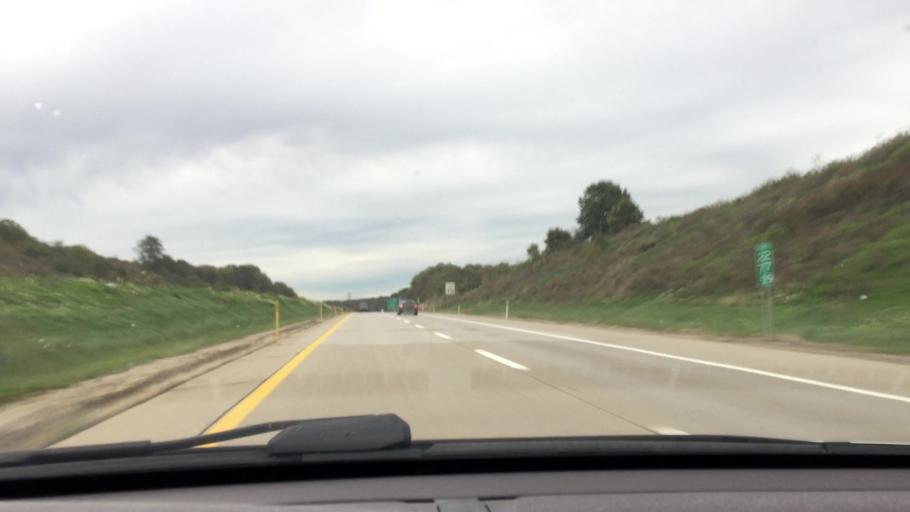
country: US
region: Pennsylvania
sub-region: Beaver County
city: Big Beaver
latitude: 40.8072
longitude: -80.3641
